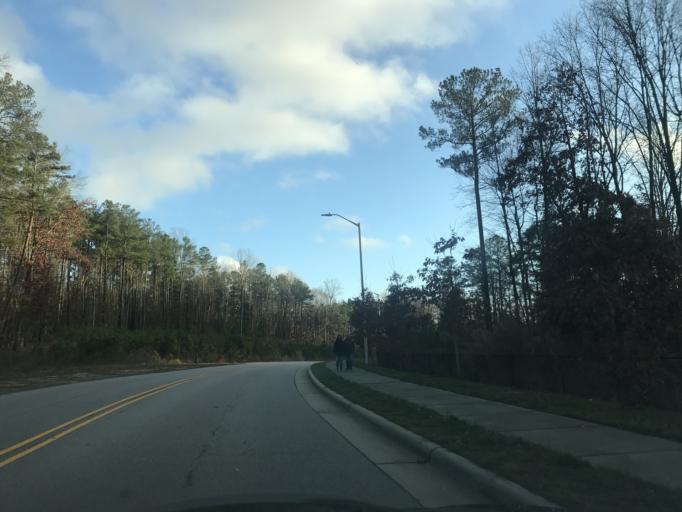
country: US
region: North Carolina
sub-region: Wake County
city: Wake Forest
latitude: 35.9558
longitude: -78.5338
